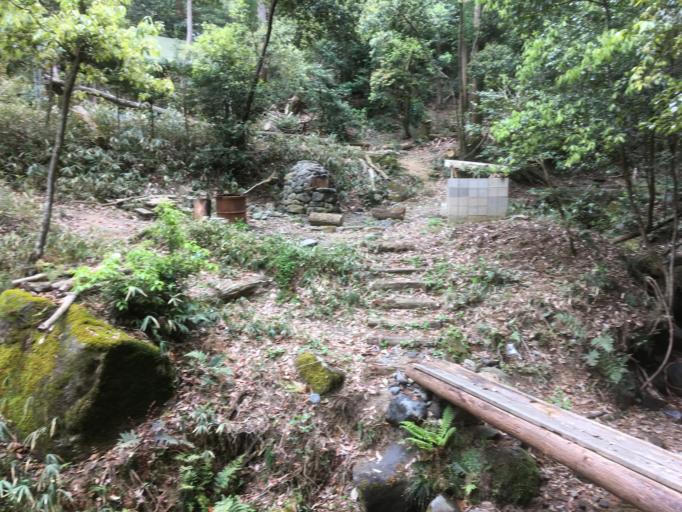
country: JP
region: Nara
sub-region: Ikoma-shi
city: Ikoma
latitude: 34.6939
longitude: 135.6886
